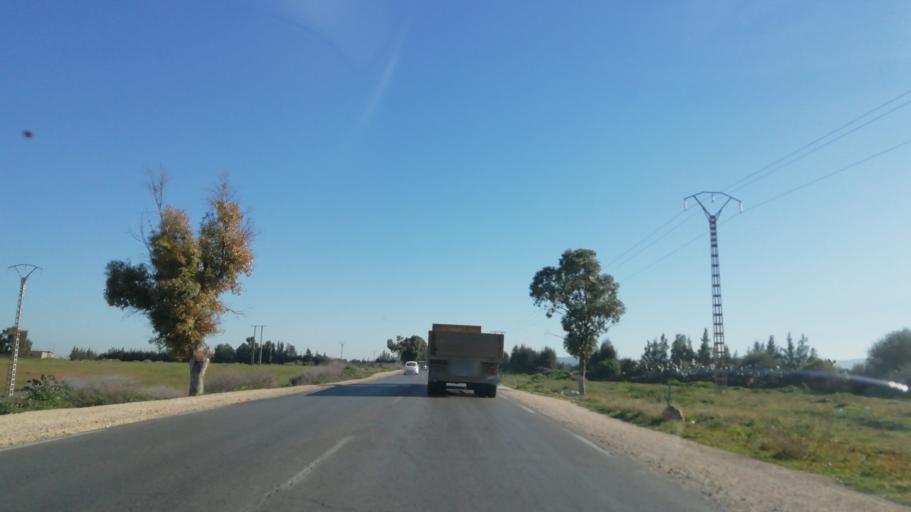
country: DZ
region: Relizane
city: Zemoura
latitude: 35.7490
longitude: 0.6912
